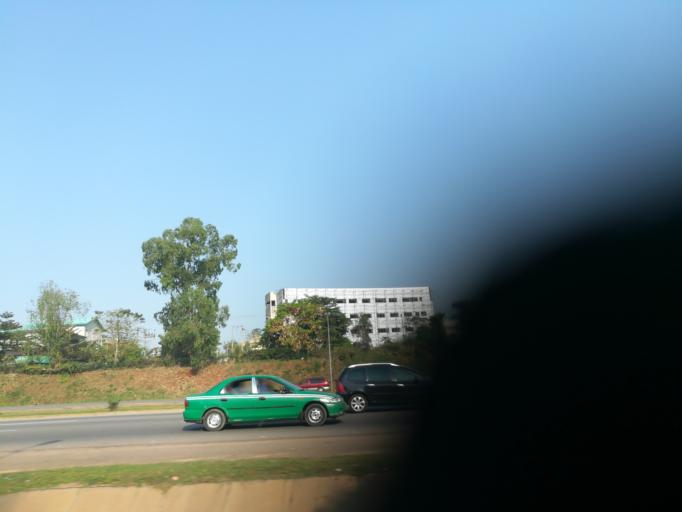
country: NG
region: Abuja Federal Capital Territory
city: Abuja
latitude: 9.0600
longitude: 7.4533
